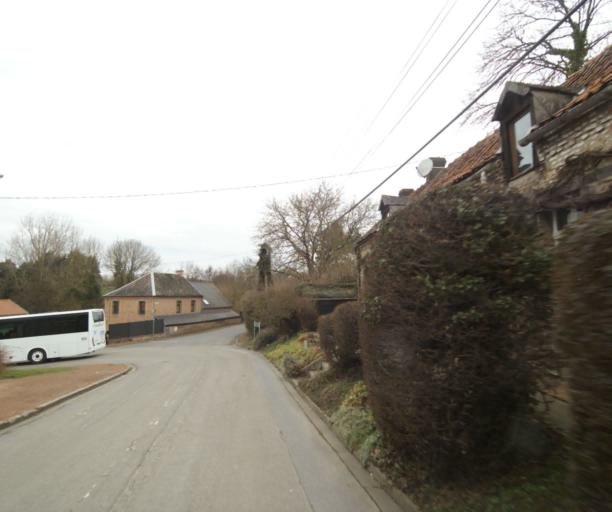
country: FR
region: Nord-Pas-de-Calais
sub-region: Departement du Nord
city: Sebourg
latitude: 50.3524
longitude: 3.6507
